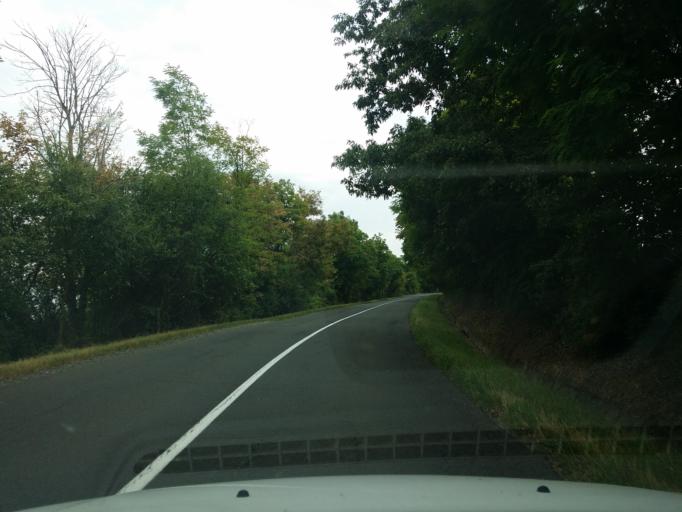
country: HU
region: Nograd
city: Bercel
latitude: 47.9396
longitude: 19.3731
